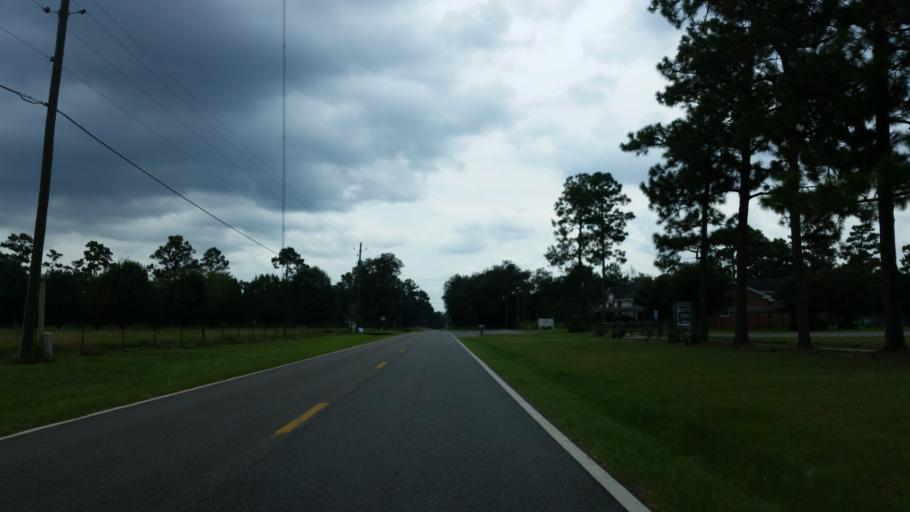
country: US
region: Florida
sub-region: Escambia County
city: Molino
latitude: 30.7128
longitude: -87.4050
